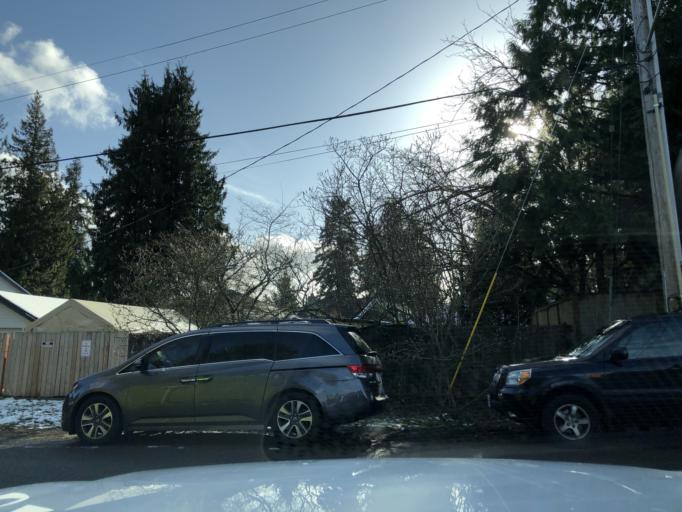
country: US
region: Washington
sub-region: King County
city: Shoreline
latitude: 47.7177
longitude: -122.3113
